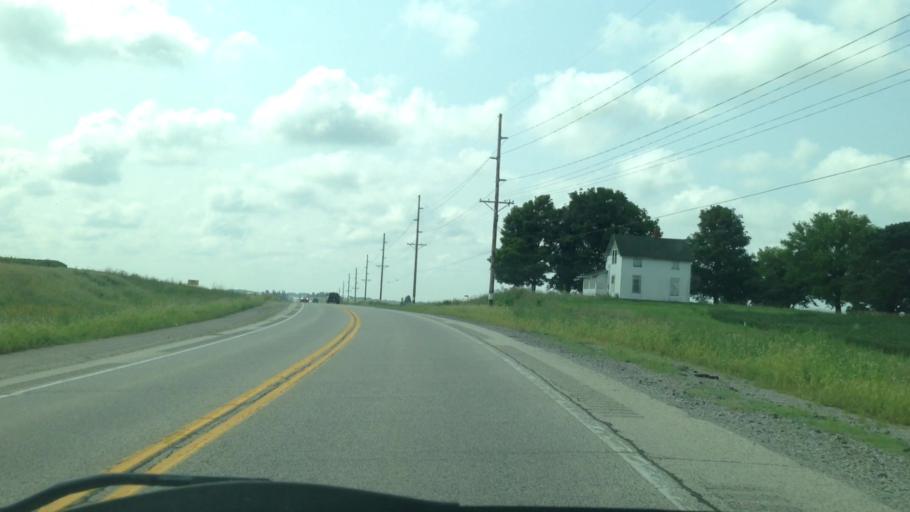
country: US
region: Iowa
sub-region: Benton County
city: Walford
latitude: 41.8723
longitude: -91.8702
